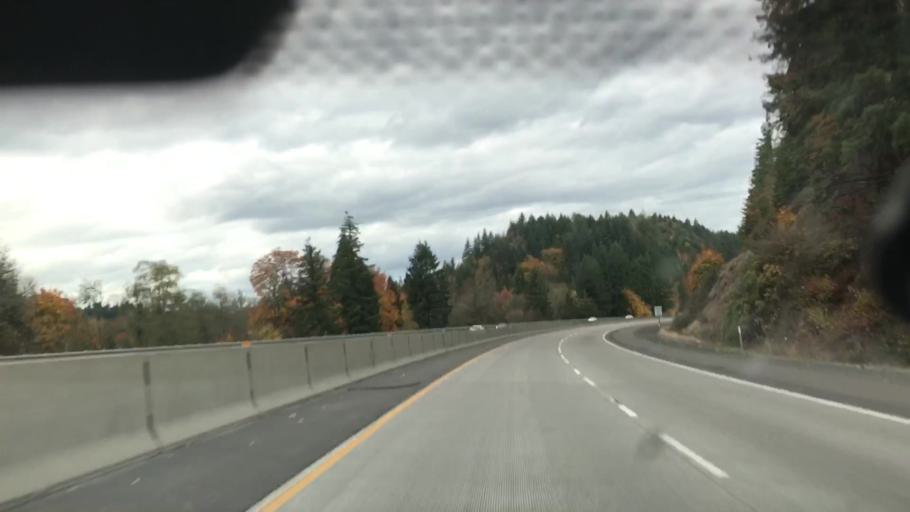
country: US
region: Oregon
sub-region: Douglas County
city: Yoncalla
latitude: 43.6285
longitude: -123.2195
